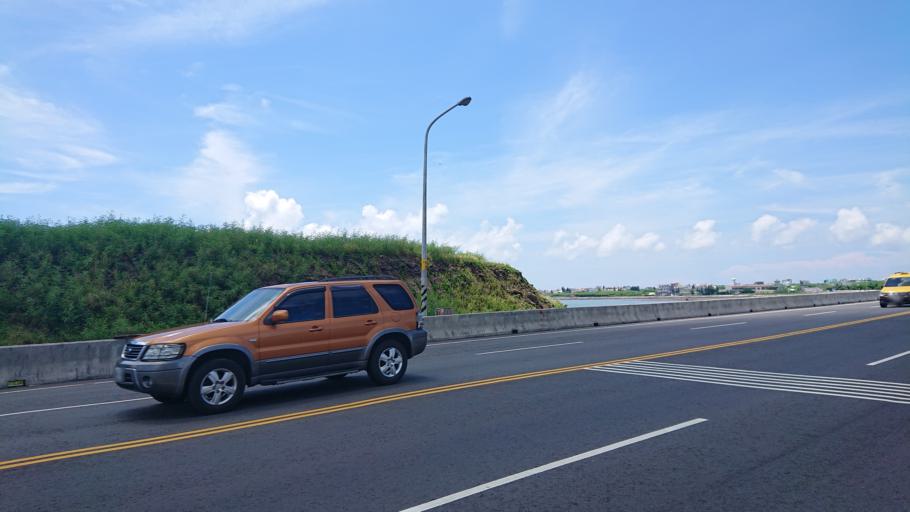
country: TW
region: Taiwan
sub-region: Penghu
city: Ma-kung
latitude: 23.6051
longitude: 119.6126
